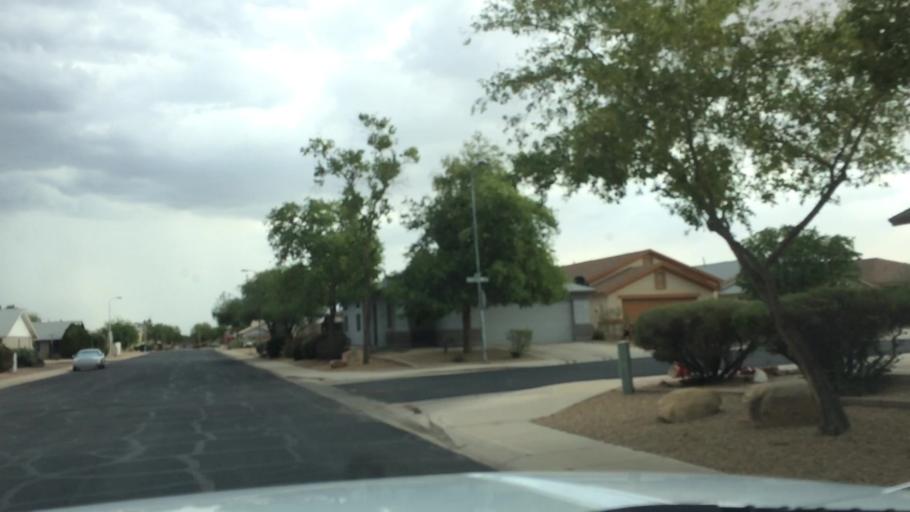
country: US
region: Arizona
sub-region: Maricopa County
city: Sun City
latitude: 33.5724
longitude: -112.2685
